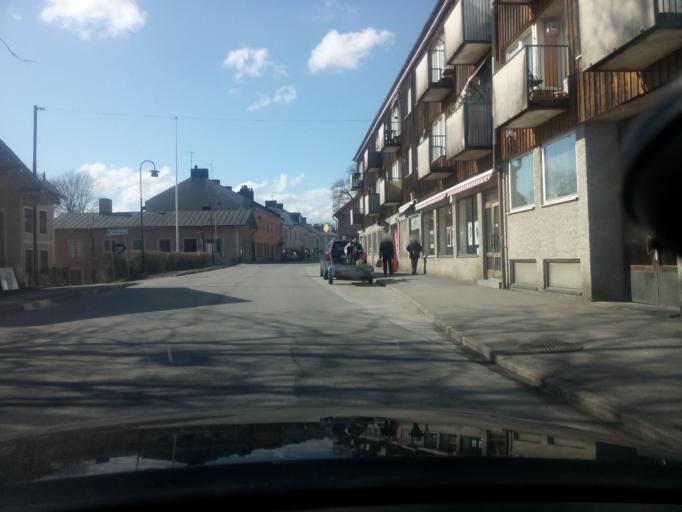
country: SE
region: Soedermanland
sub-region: Flens Kommun
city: Malmkoping
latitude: 59.1323
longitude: 16.7292
